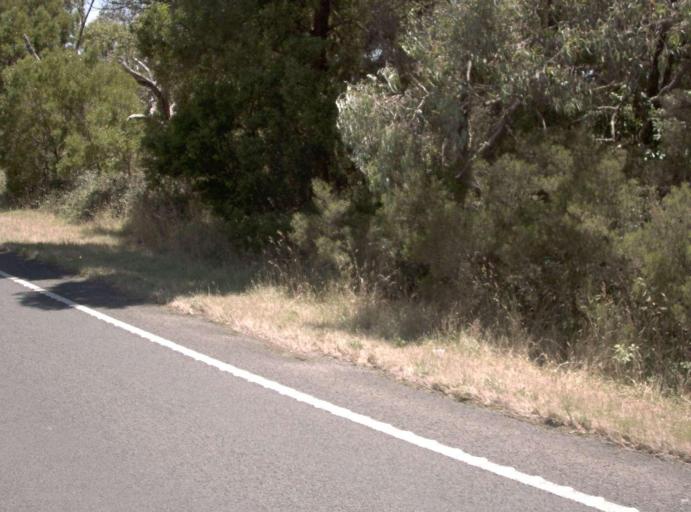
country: AU
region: Victoria
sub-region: Cardinia
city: Bunyip
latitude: -38.0771
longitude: 145.7337
